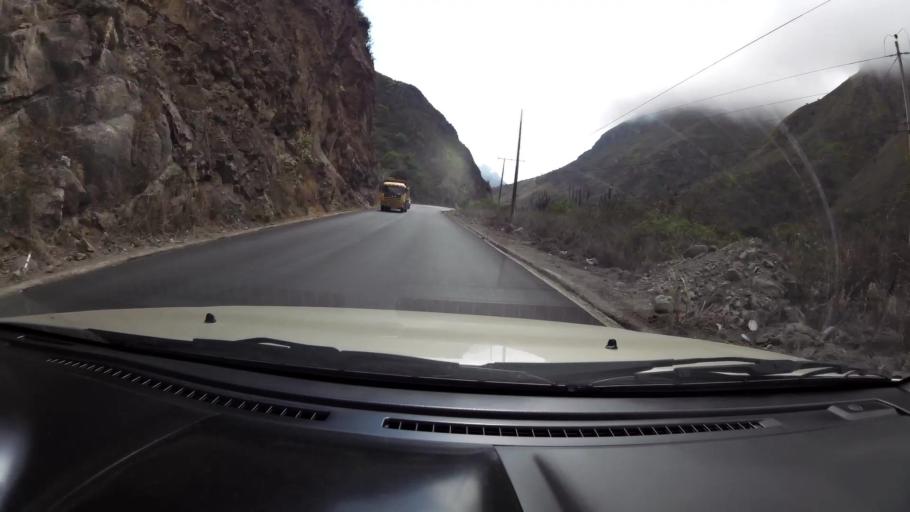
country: EC
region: El Oro
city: Pasaje
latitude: -3.3135
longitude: -79.4927
